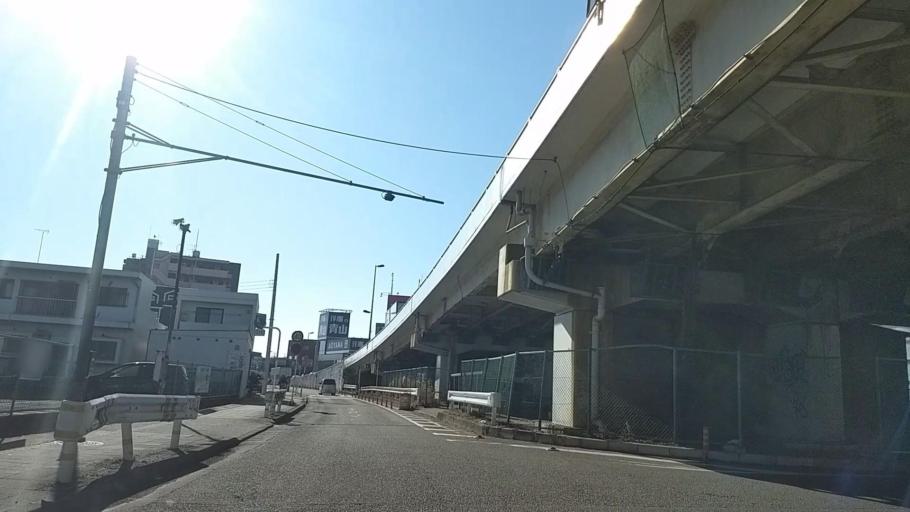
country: JP
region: Tokyo
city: Hachioji
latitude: 35.5978
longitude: 139.3388
